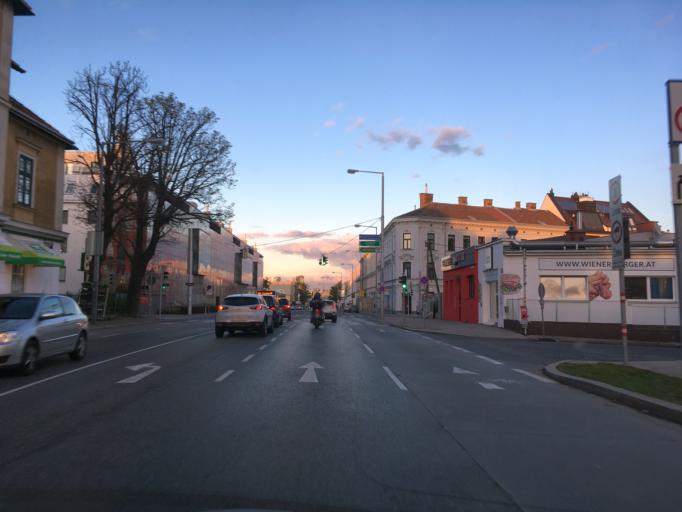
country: AT
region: Lower Austria
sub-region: Politischer Bezirk Modling
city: Vosendorf
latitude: 48.1591
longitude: 16.3081
